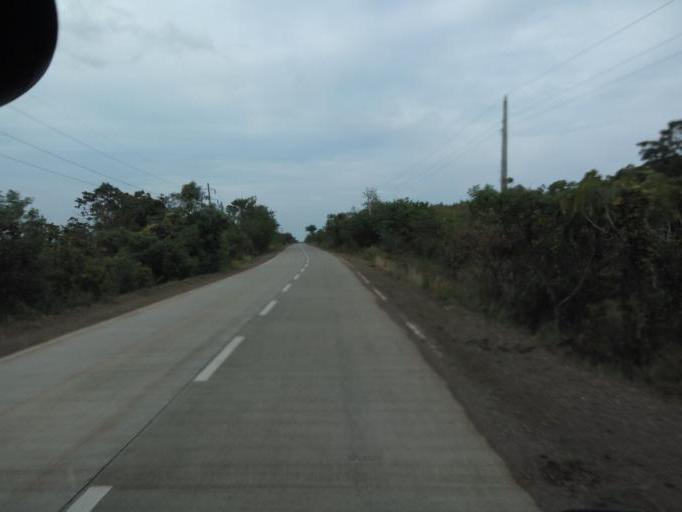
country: PH
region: Cagayan Valley
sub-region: Province of Cagayan
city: Magapit
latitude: 18.1670
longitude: 121.7452
